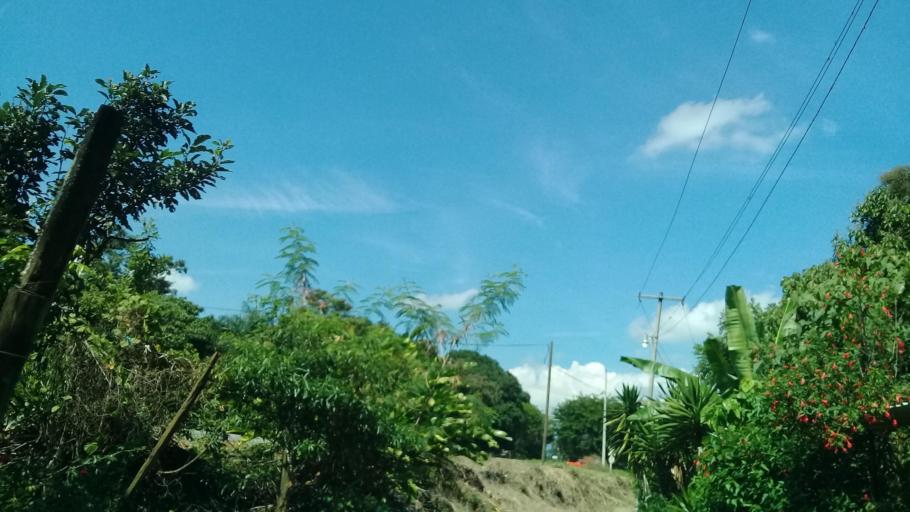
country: MX
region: Veracruz
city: Amatlan de los Reyes
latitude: 18.8373
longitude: -96.9214
